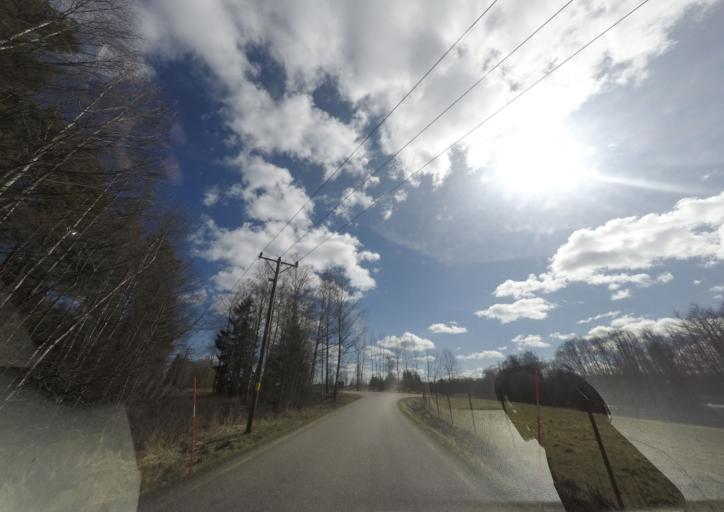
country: SE
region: OEstergoetland
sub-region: Norrkopings Kommun
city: Krokek
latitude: 58.7455
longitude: 16.4671
